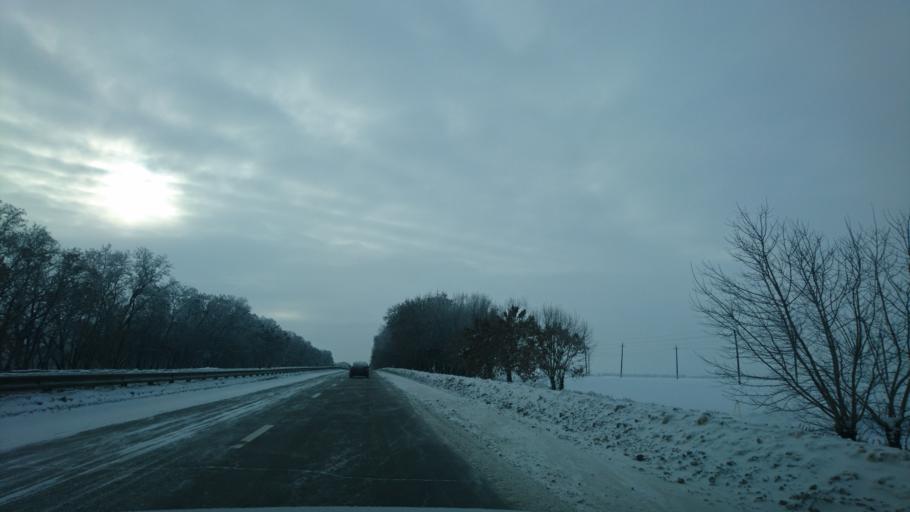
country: RU
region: Belgorod
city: Mayskiy
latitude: 50.4791
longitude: 36.4059
